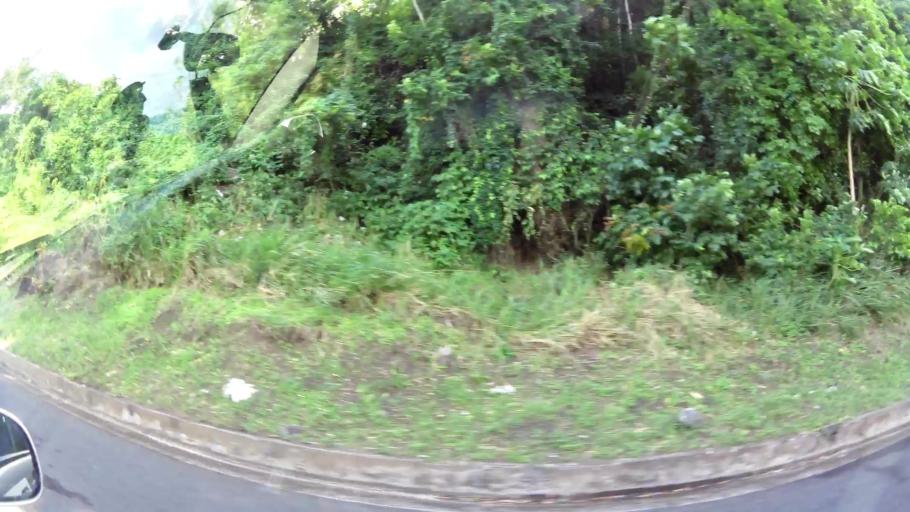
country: GD
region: Saint Mark
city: Victoria
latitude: 12.2175
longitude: -61.6875
